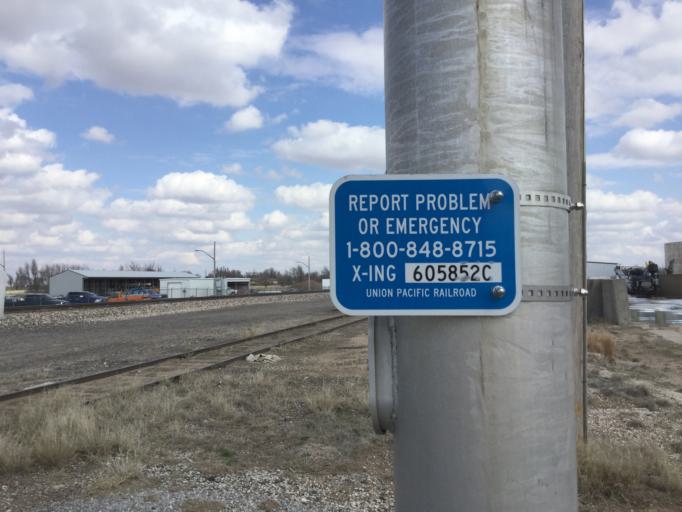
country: US
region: Kansas
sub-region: Kiowa County
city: Greensburg
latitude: 37.6092
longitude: -99.2928
